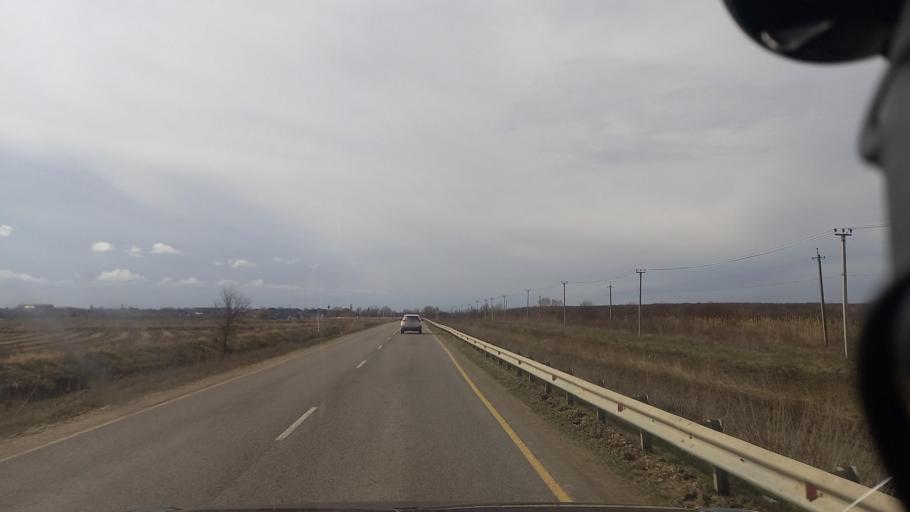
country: RU
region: Adygeya
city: Takhtamukay
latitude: 44.9410
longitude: 38.9891
